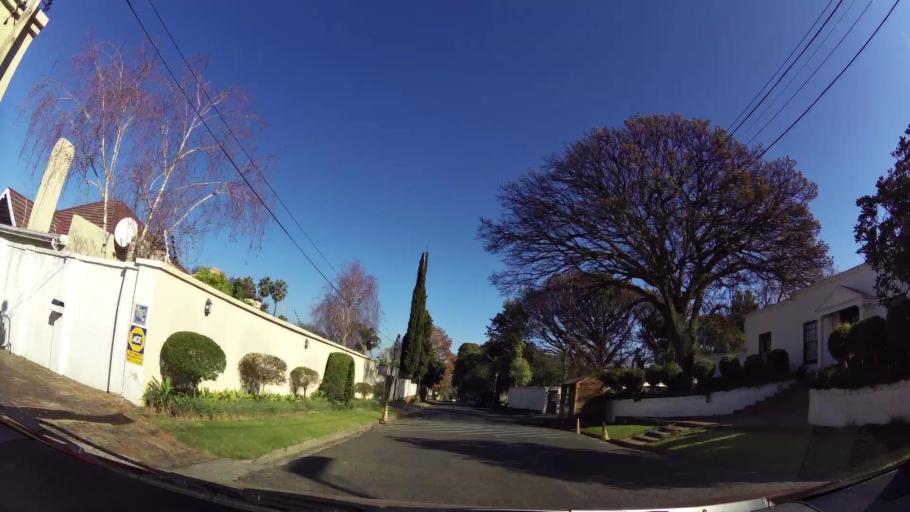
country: ZA
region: Gauteng
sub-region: City of Johannesburg Metropolitan Municipality
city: Johannesburg
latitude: -26.1479
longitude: 28.0268
